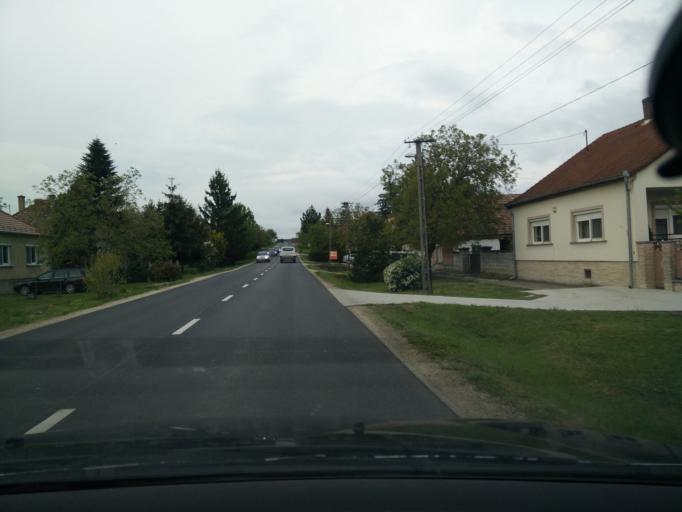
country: HU
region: Gyor-Moson-Sopron
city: Tet
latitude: 47.4634
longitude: 17.4886
